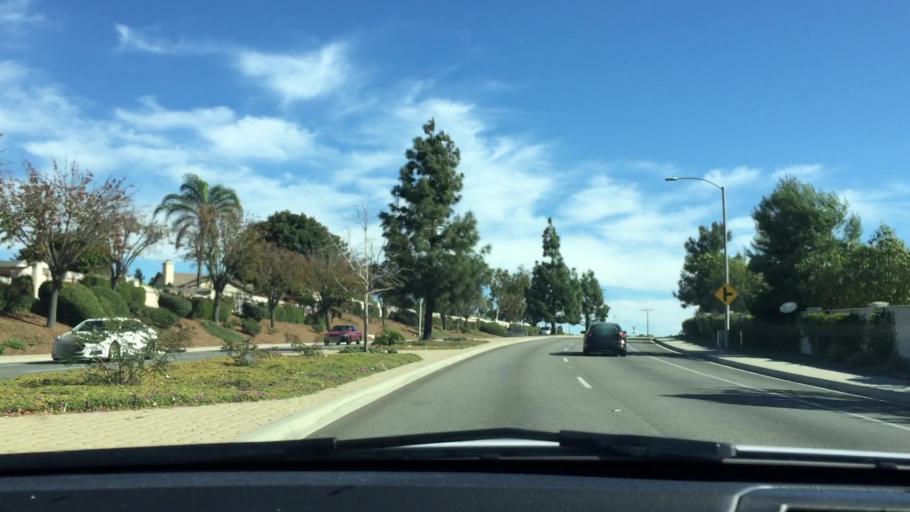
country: US
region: California
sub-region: San Diego County
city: Vista
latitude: 33.2388
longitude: -117.2667
